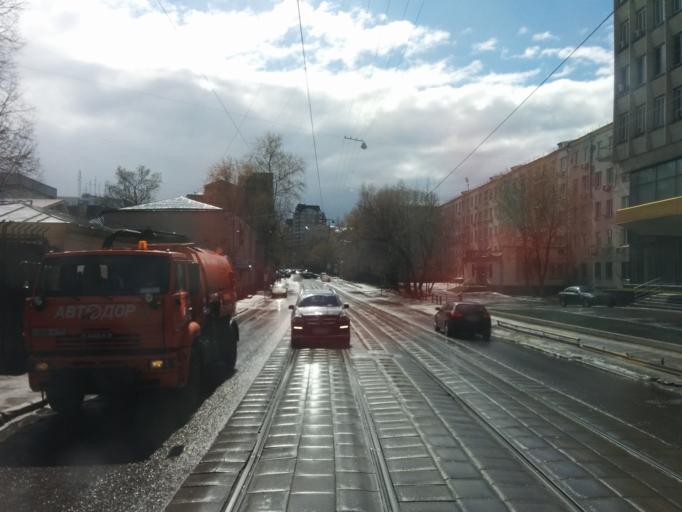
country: RU
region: Moscow
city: Mar'ina Roshcha
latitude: 55.7798
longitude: 37.6310
